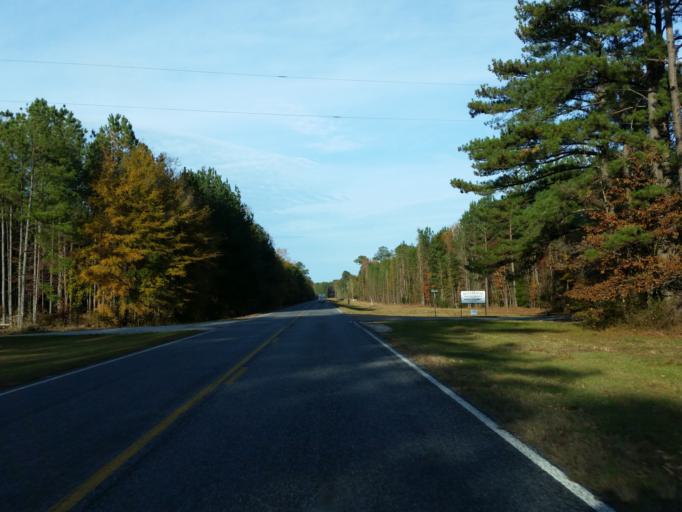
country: US
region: Mississippi
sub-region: Clarke County
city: Stonewall
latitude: 32.0738
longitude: -88.8772
